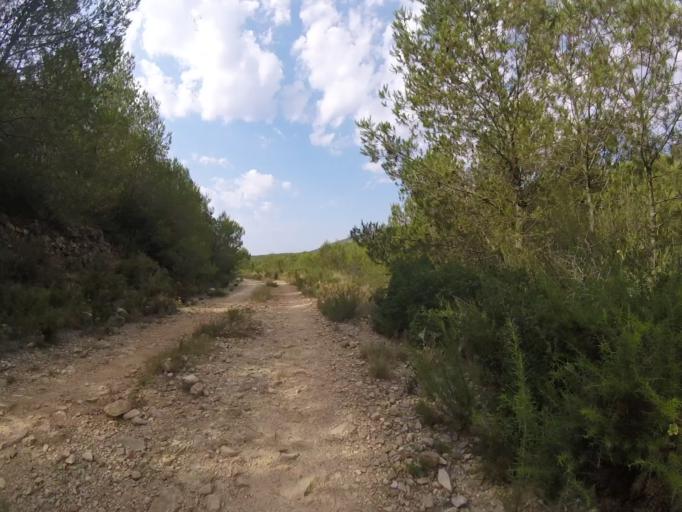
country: ES
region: Valencia
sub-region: Provincia de Castello
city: Alcala de Xivert
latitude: 40.3582
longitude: 0.1987
